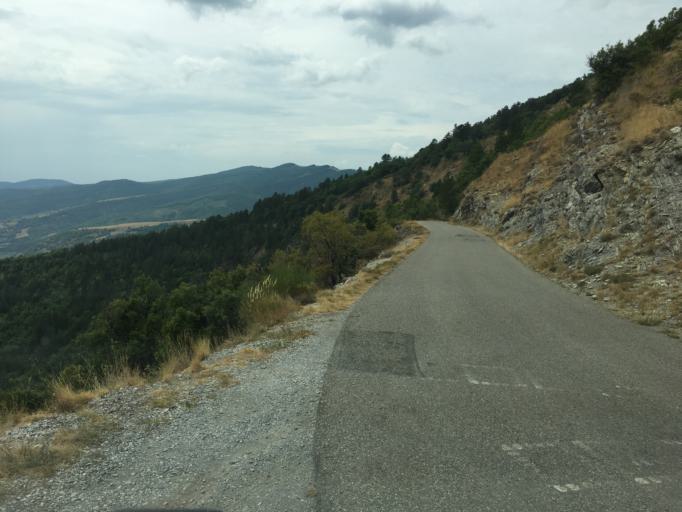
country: FR
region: Provence-Alpes-Cote d'Azur
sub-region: Departement des Alpes-de-Haute-Provence
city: Digne-les-Bains
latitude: 44.2012
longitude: 6.1511
